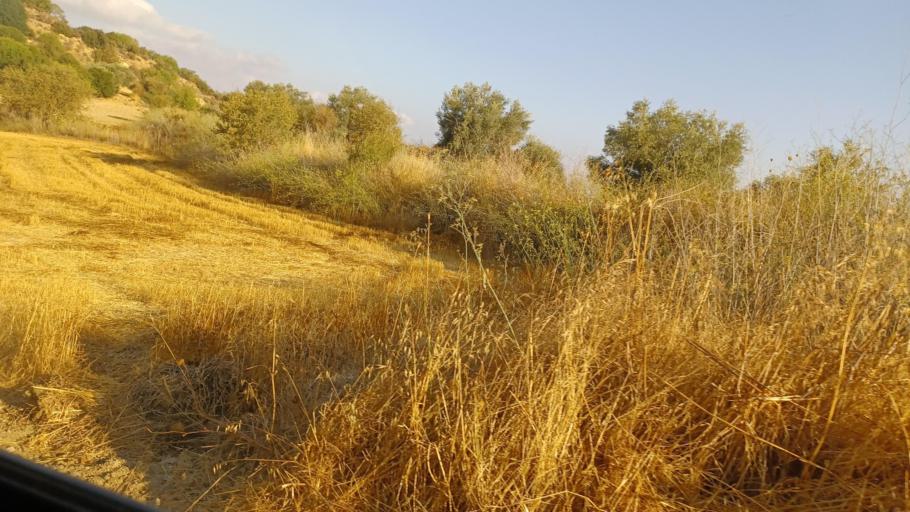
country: CY
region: Pafos
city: Tala
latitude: 34.9244
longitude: 32.4975
